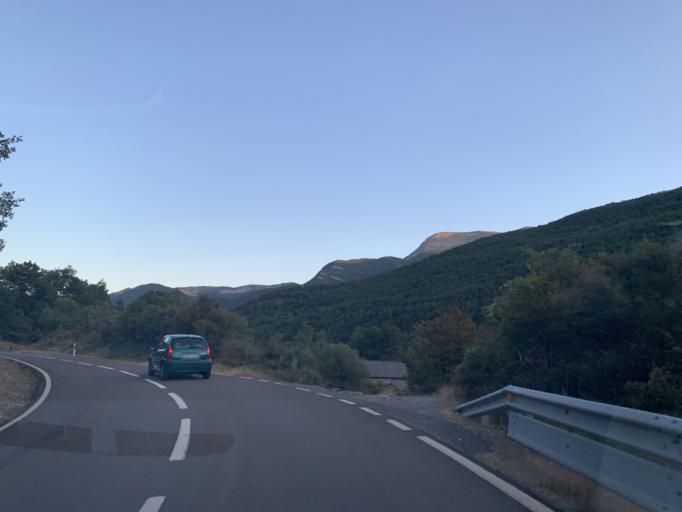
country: ES
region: Aragon
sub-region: Provincia de Huesca
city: Fiscal
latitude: 42.5115
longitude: -0.1266
